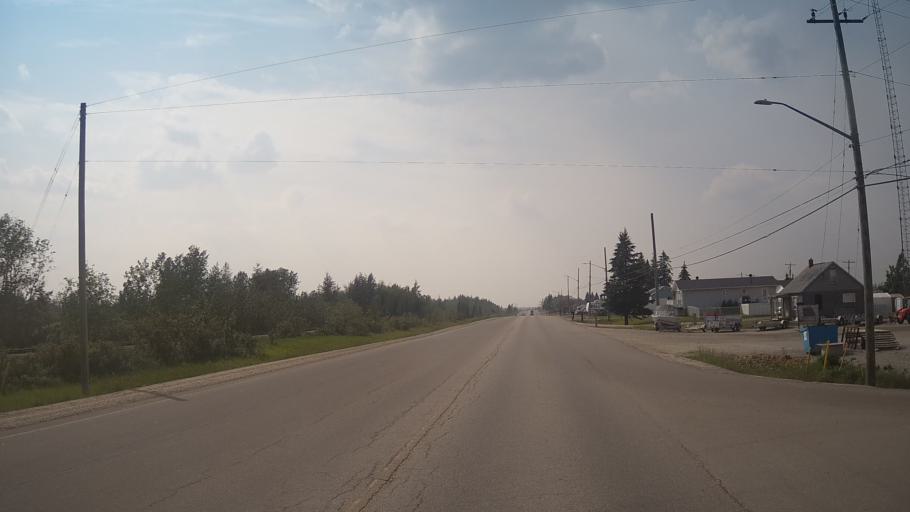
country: CA
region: Ontario
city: Kapuskasing
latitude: 49.4010
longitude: -82.3806
